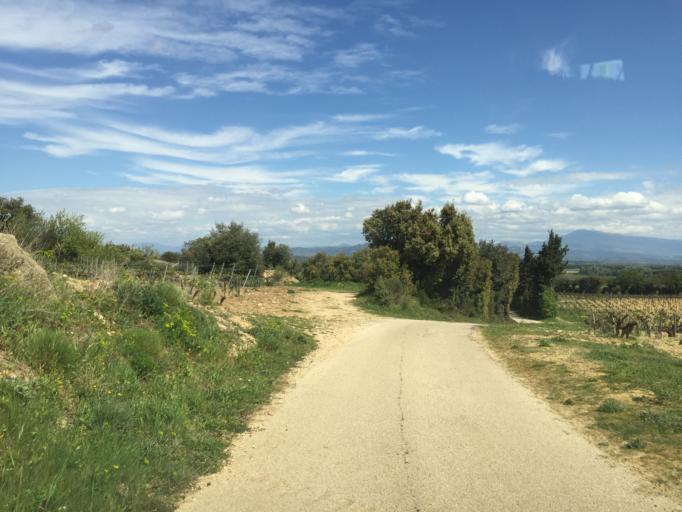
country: FR
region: Provence-Alpes-Cote d'Azur
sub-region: Departement du Vaucluse
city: Courthezon
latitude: 44.0663
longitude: 4.8661
